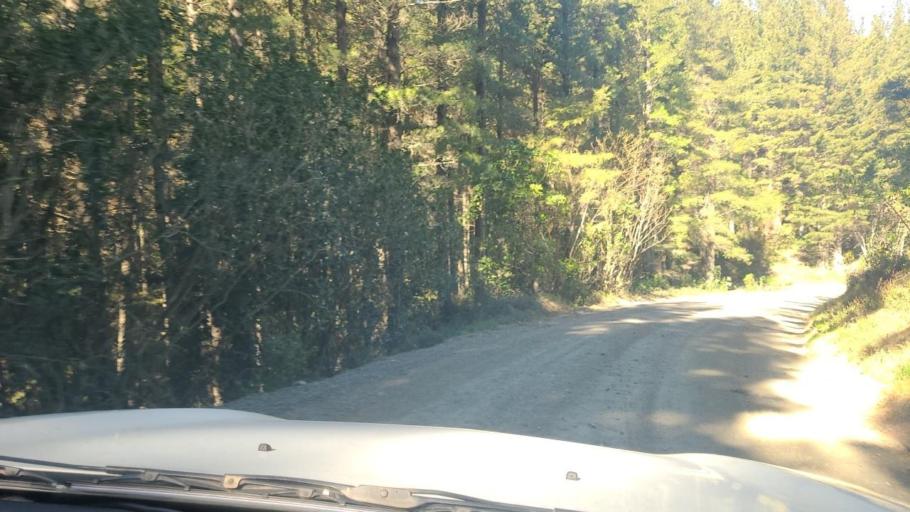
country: NZ
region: Hawke's Bay
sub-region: Napier City
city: Taradale
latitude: -39.4111
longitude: 176.4863
